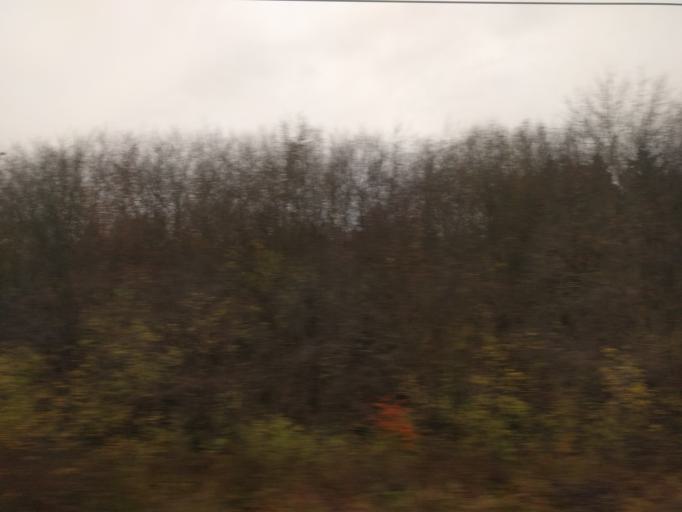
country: DK
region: Zealand
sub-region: Soro Kommune
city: Frederiksberg
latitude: 55.4339
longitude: 11.6309
